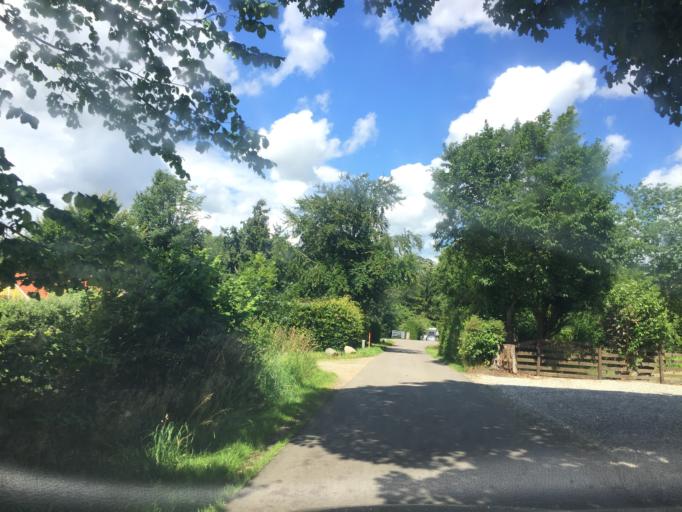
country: DK
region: Capital Region
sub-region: Egedal Kommune
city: Smorumnedre
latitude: 55.7024
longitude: 12.2698
